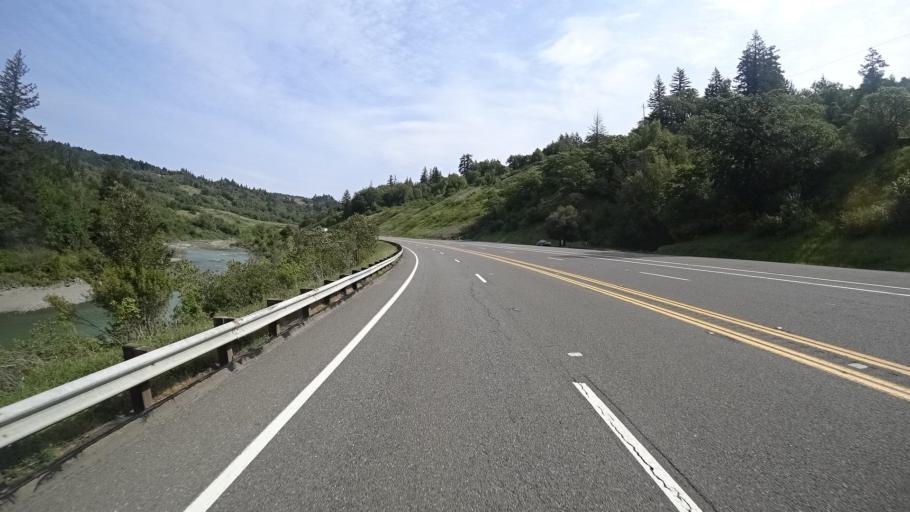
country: US
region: California
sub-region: Humboldt County
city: Redway
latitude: 40.1510
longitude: -123.7956
